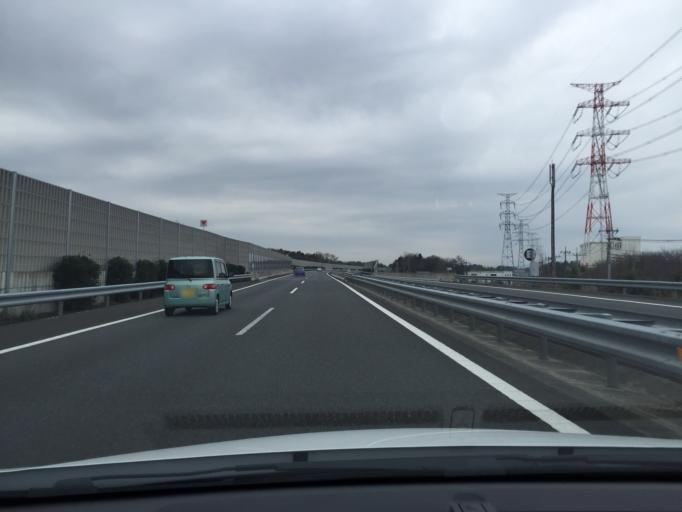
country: JP
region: Saitama
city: Sakado
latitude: 35.9549
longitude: 139.4287
